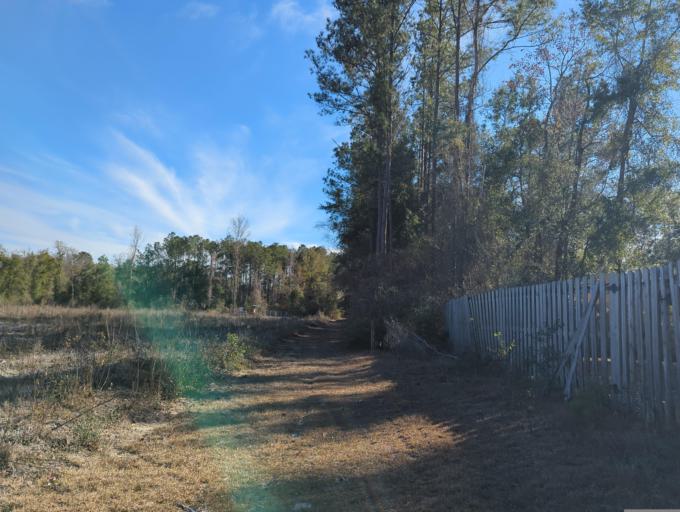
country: US
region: Florida
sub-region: Wakulla County
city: Crawfordville
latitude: 30.1838
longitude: -84.3351
